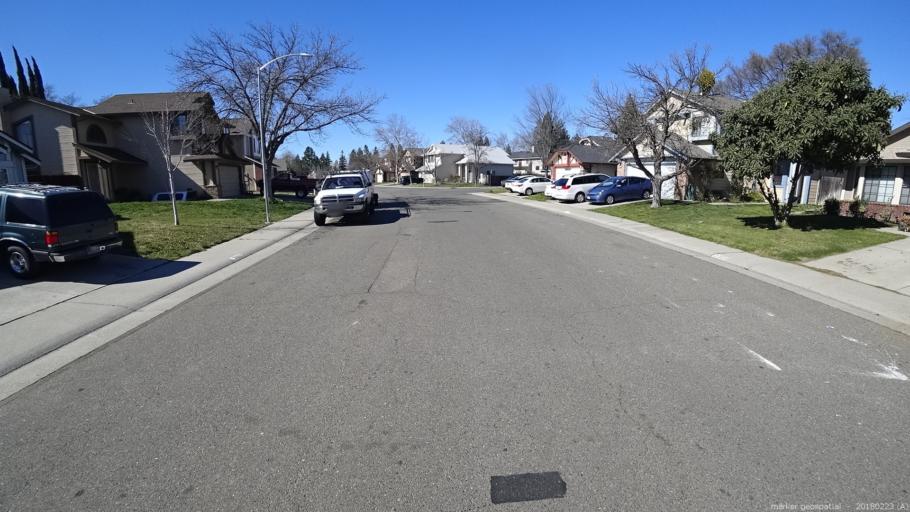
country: US
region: California
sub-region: Sacramento County
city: North Highlands
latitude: 38.7158
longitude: -121.3850
